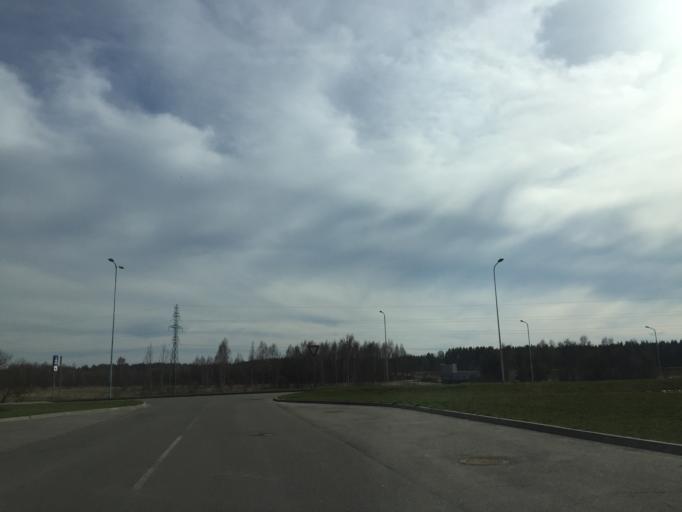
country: LV
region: Ogre
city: Ogre
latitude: 56.8175
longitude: 24.5783
